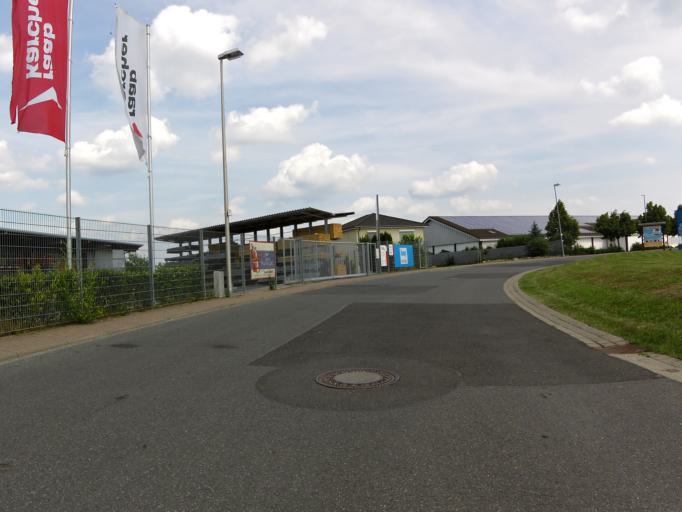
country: DE
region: Bavaria
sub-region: Regierungsbezirk Unterfranken
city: Eisingen
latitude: 49.7621
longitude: 9.8443
